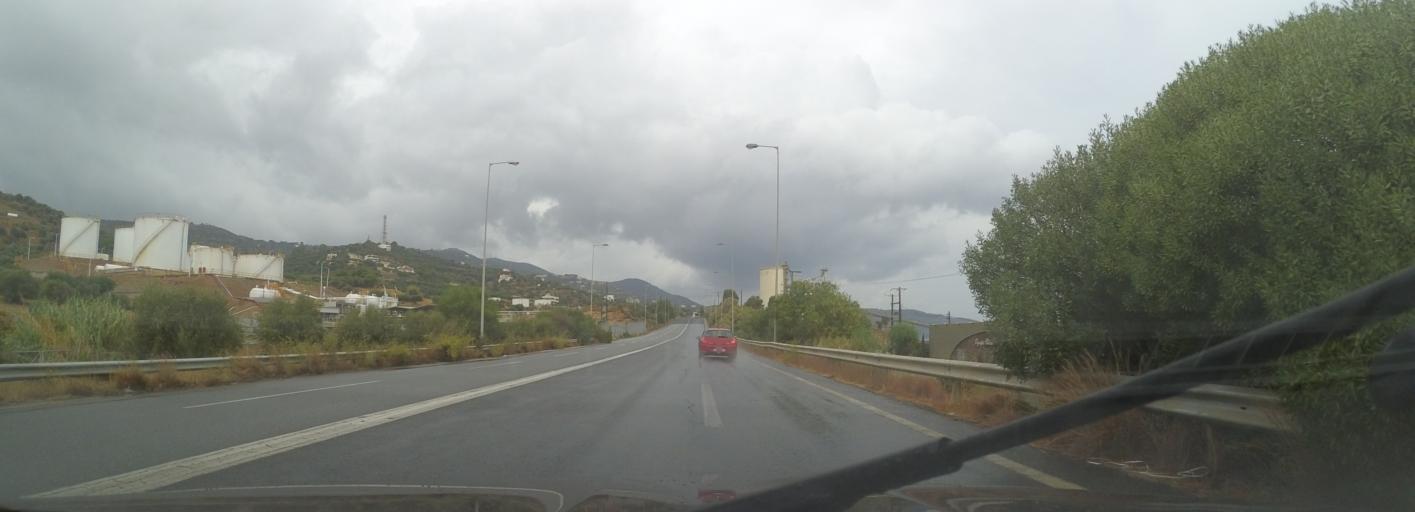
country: GR
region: Crete
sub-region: Nomos Irakleiou
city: Gazi
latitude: 35.3434
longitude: 25.0471
